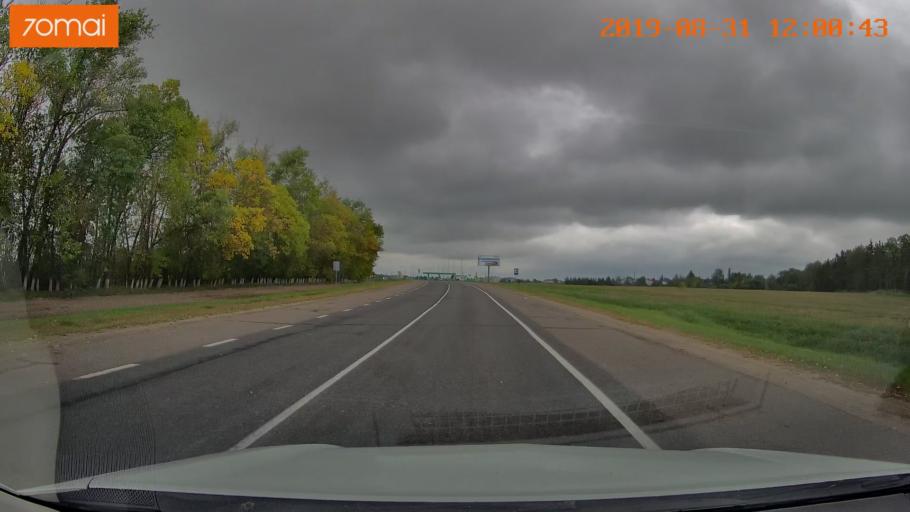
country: BY
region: Mogilev
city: Horad Krychaw
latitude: 53.6814
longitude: 31.6837
